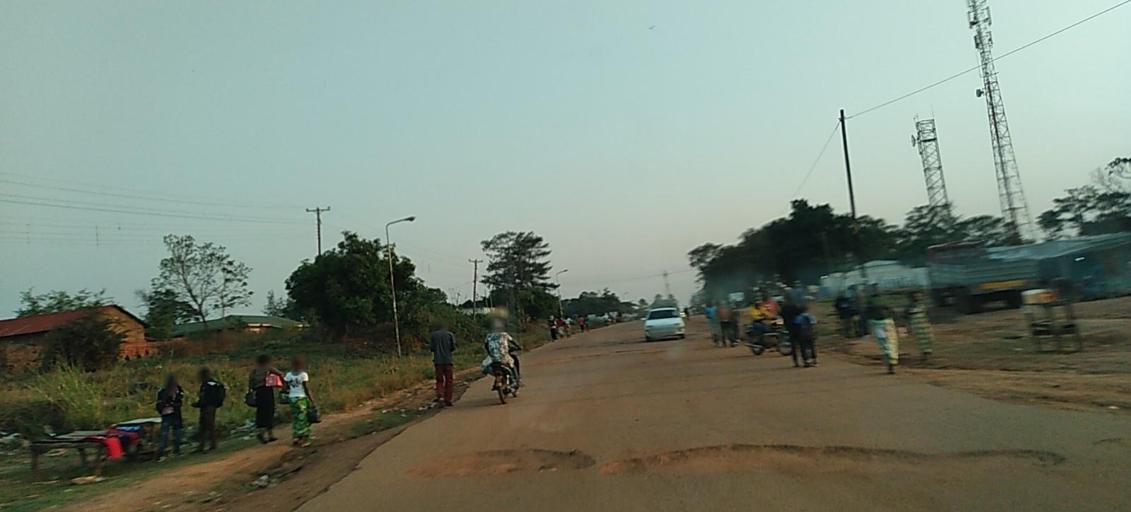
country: ZM
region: North-Western
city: Mwinilunga
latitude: -11.7327
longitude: 24.4311
